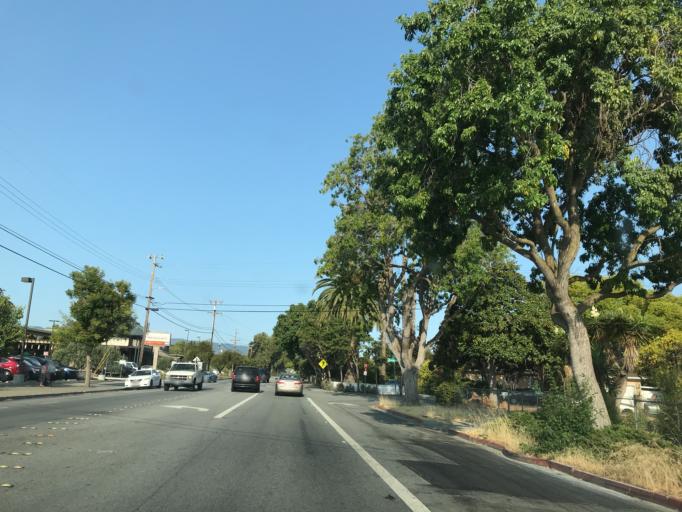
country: US
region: California
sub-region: San Mateo County
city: North Fair Oaks
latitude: 37.4788
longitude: -122.1870
